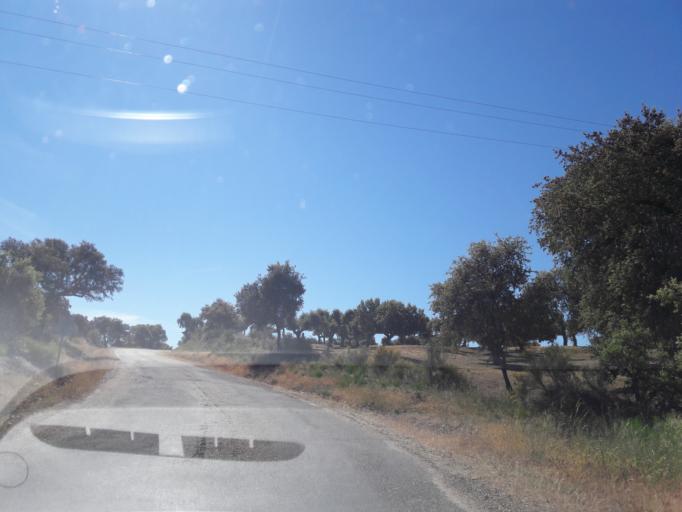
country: ES
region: Castille and Leon
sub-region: Provincia de Salamanca
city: Juzbado
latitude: 41.0643
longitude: -5.8986
